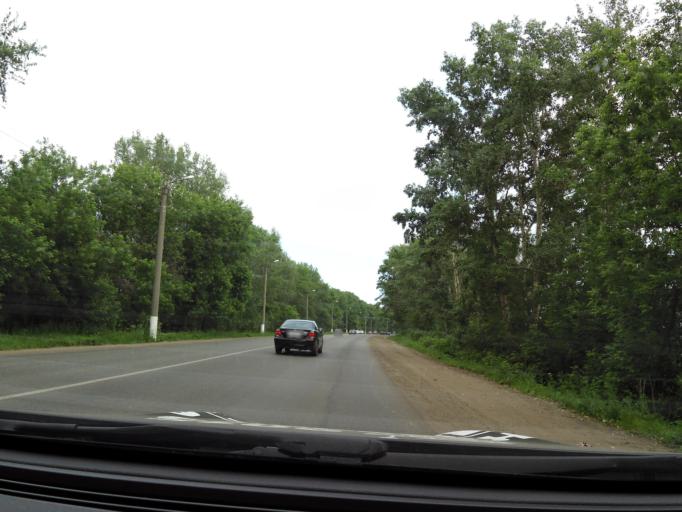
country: RU
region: Kirov
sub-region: Kirovo-Chepetskiy Rayon
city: Kirov
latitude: 58.6190
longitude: 49.7222
